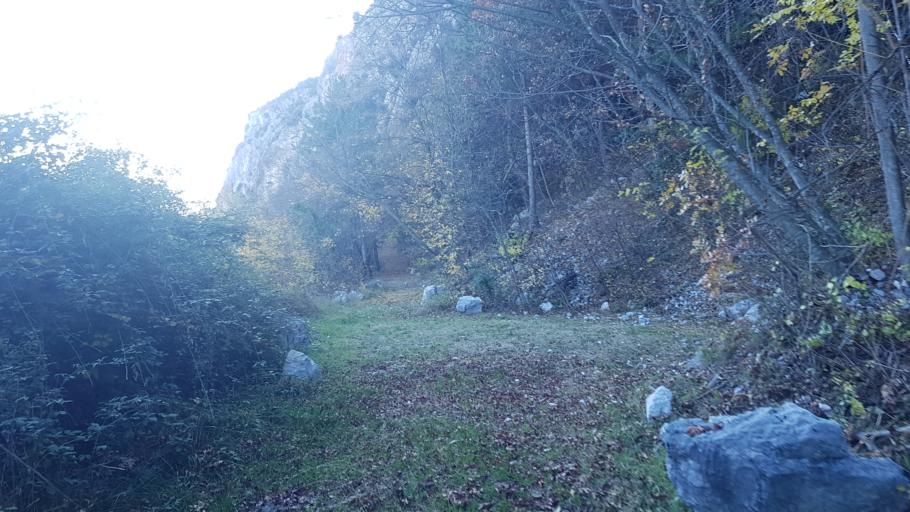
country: IT
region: Trentino-Alto Adige
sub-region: Provincia di Trento
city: Vezzano
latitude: 46.0758
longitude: 10.9813
